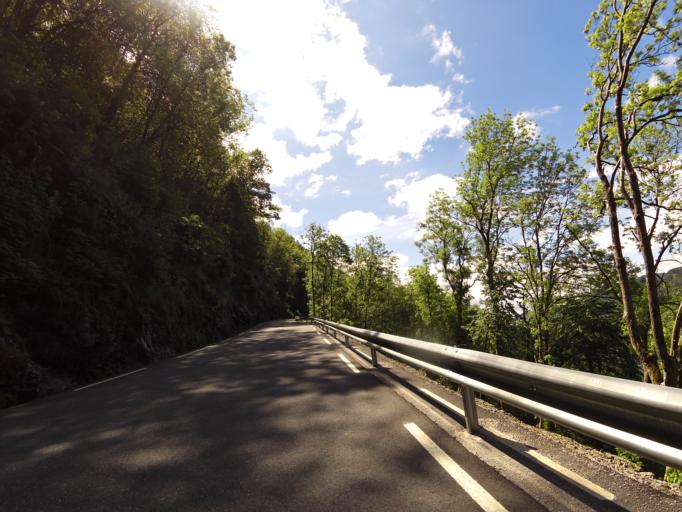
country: NO
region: Vest-Agder
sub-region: Kvinesdal
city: Liknes
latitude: 58.2986
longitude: 6.9508
